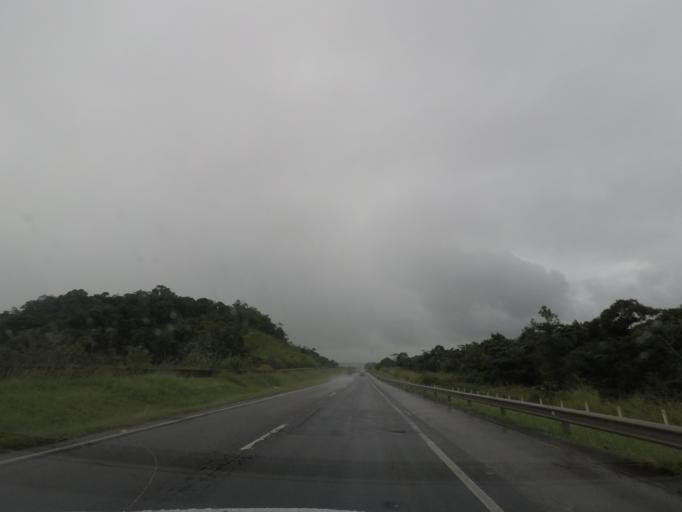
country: BR
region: Sao Paulo
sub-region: Registro
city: Registro
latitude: -24.4387
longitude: -47.7953
